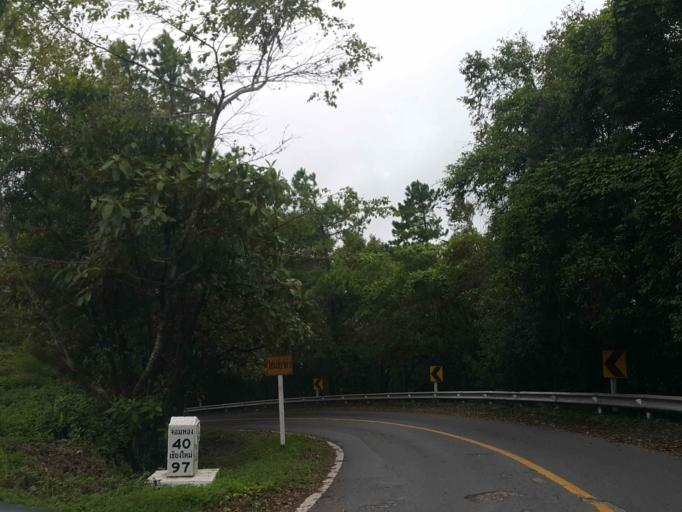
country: TH
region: Chiang Mai
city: Mae Chaem
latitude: 18.5435
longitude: 98.4876
